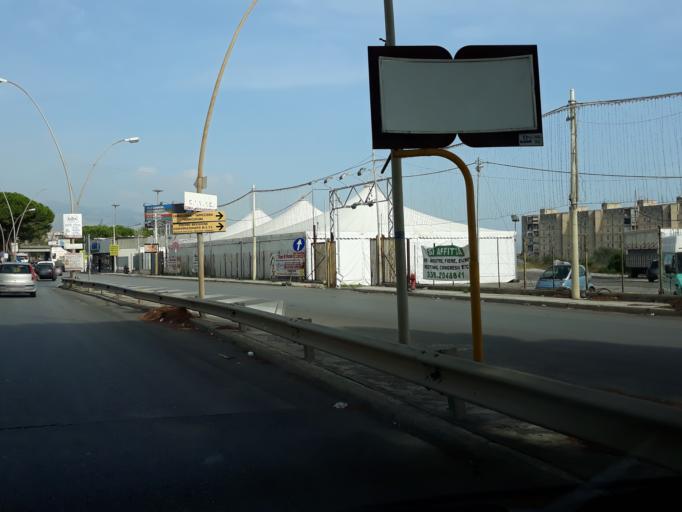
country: IT
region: Sicily
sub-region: Palermo
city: Villa Ciambra
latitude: 38.0916
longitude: 13.3423
